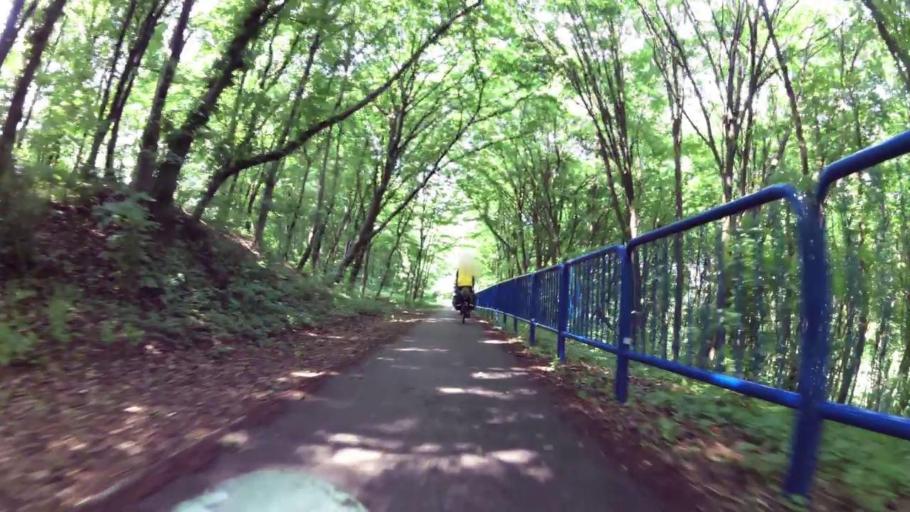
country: PL
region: Kujawsko-Pomorskie
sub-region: Powiat bydgoski
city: Koronowo
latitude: 53.2965
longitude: 17.9477
